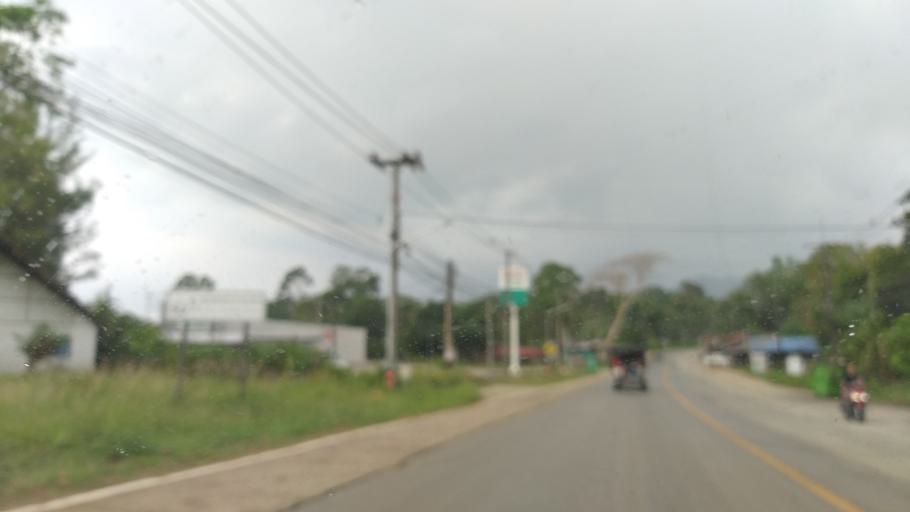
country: TH
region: Trat
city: Ko Chang Tai
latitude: 12.0843
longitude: 102.2788
